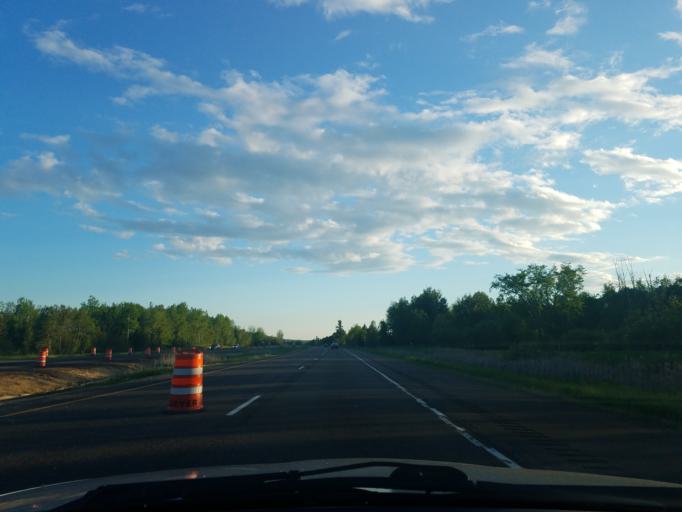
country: US
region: Minnesota
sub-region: Carlton County
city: Carlton
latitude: 46.6227
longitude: -92.5386
